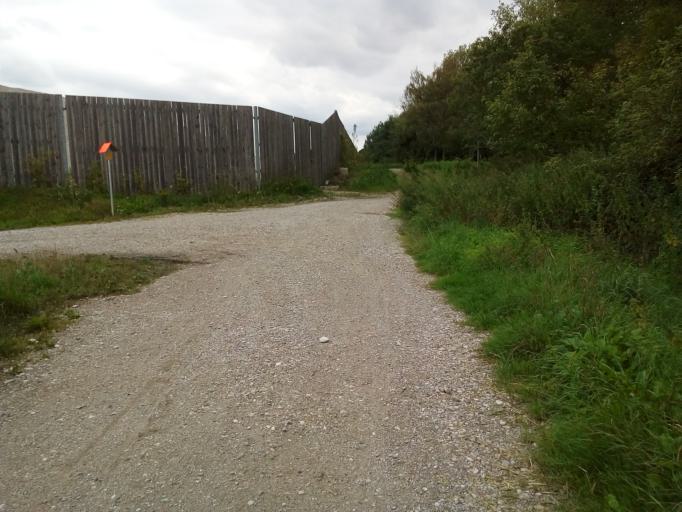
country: DE
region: Bavaria
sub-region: Upper Bavaria
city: Aschheim
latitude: 48.1616
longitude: 11.6856
